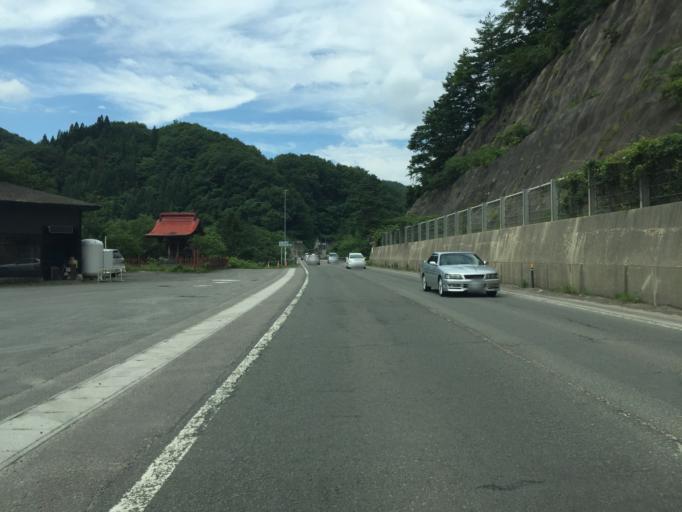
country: JP
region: Fukushima
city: Fukushima-shi
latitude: 37.8395
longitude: 140.3711
